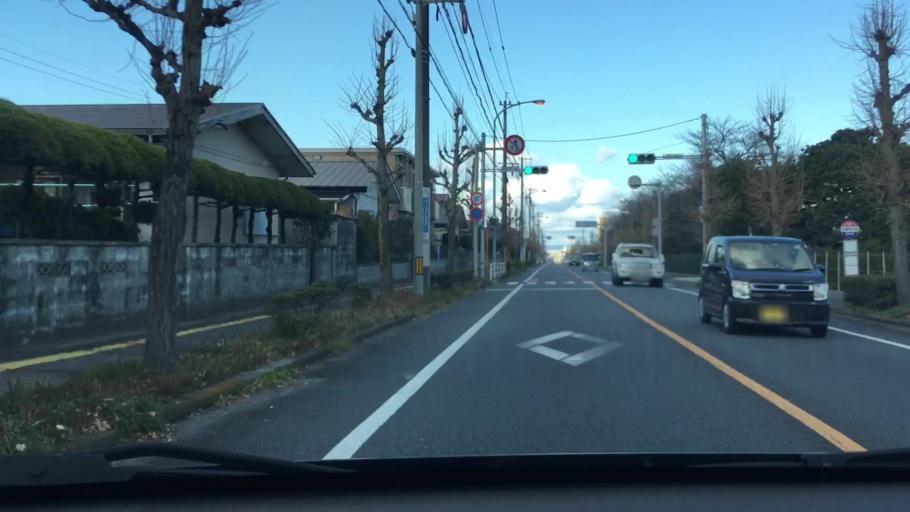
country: JP
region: Oita
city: Tsurusaki
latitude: 33.2153
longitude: 131.6588
